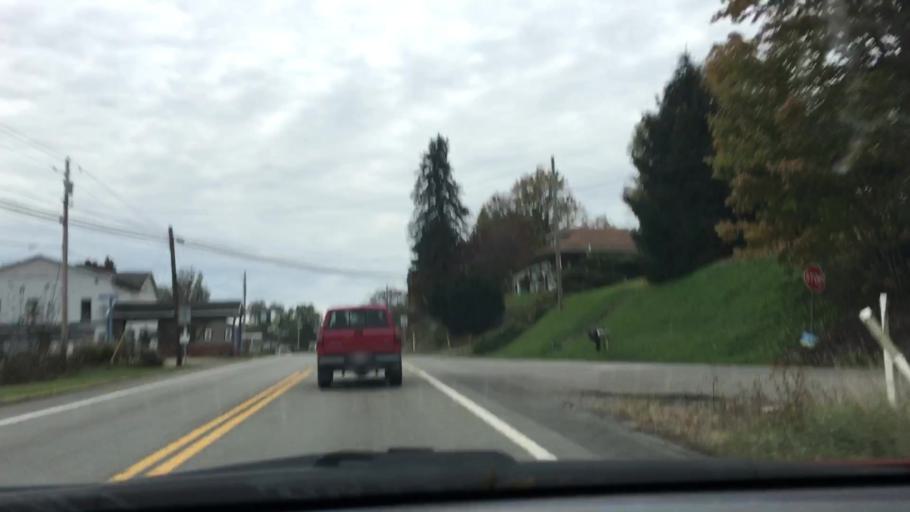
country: US
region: Pennsylvania
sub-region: Armstrong County
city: Orchard Hills
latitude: 40.5869
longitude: -79.5314
